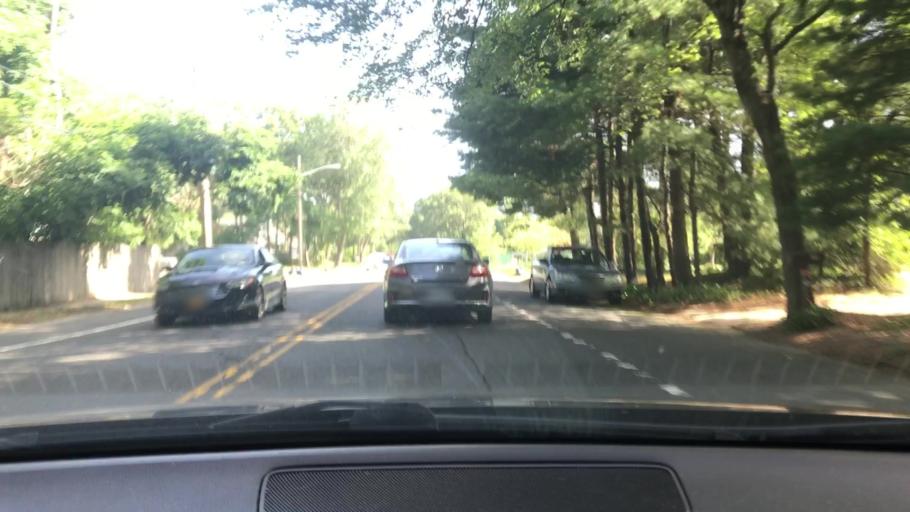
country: US
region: New York
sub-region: Suffolk County
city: Holbrook
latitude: 40.8212
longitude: -73.0799
